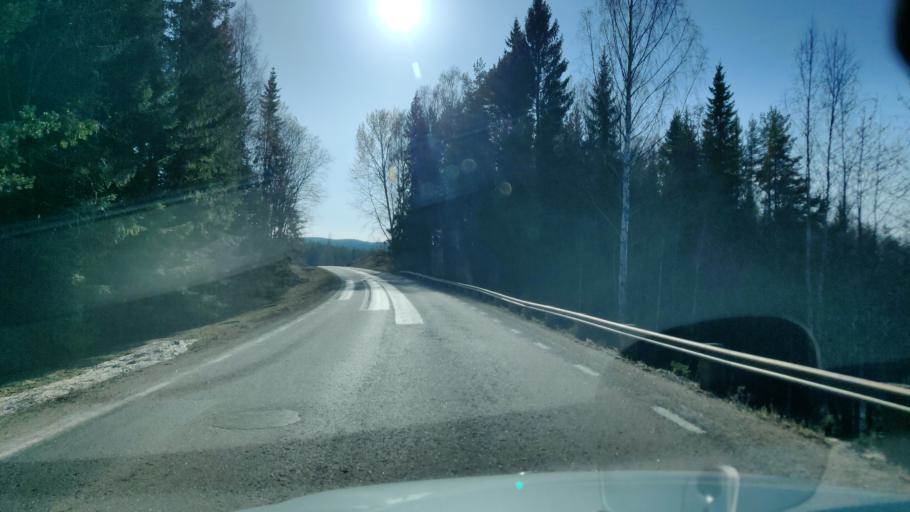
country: SE
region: Vaermland
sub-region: Sunne Kommun
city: Sunne
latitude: 59.9870
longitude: 13.3306
